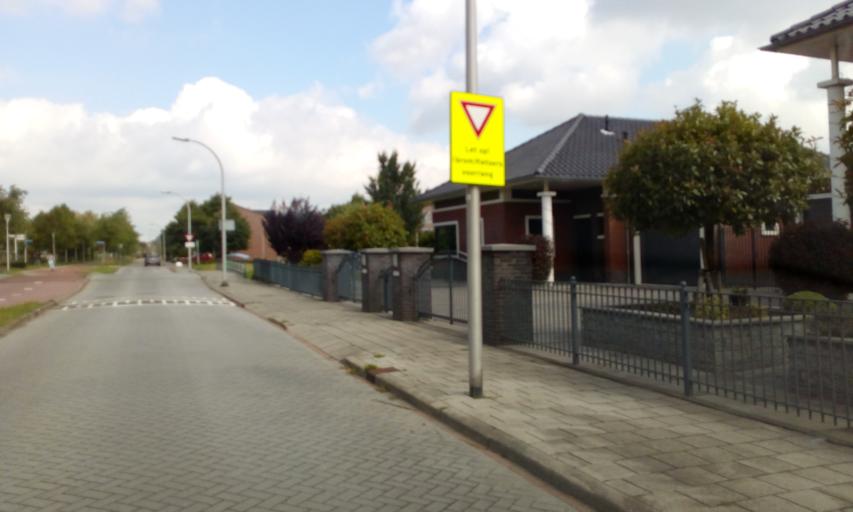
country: NL
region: South Holland
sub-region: Gemeente Pijnacker-Nootdorp
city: Pijnacker
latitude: 52.0011
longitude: 4.3969
